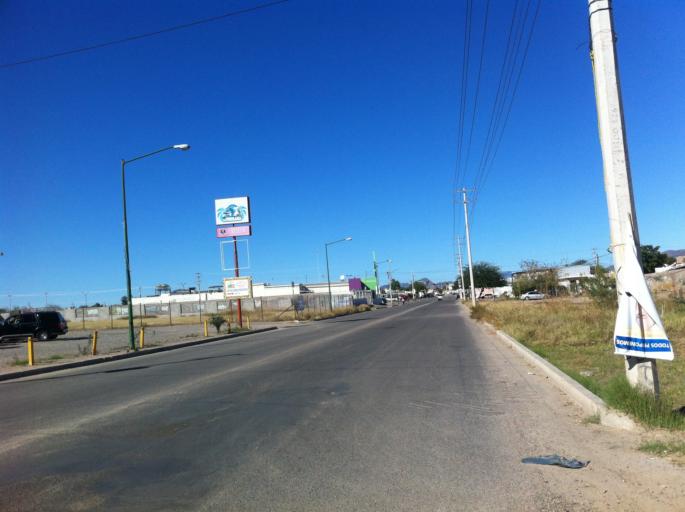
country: MX
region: Sonora
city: Hermosillo
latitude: 29.1140
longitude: -111.0055
